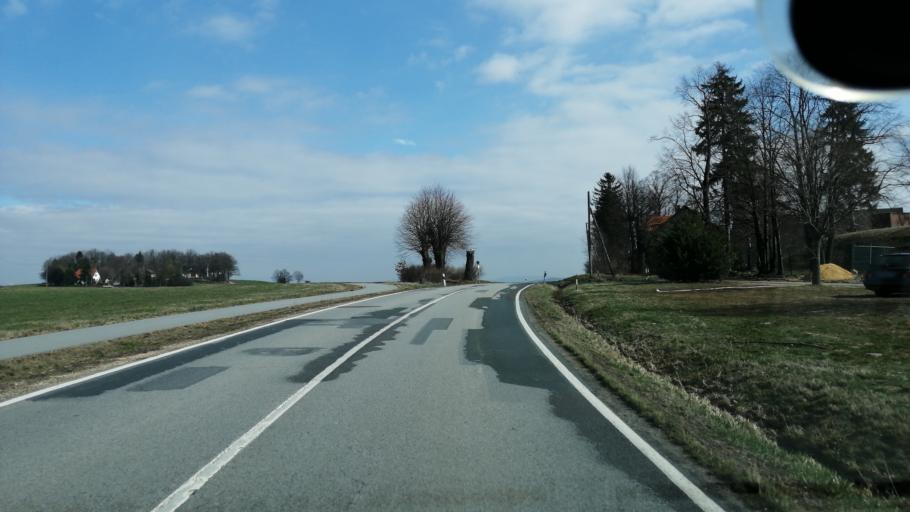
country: DE
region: Saxony
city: Grossschweidnitz
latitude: 51.0858
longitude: 14.6344
